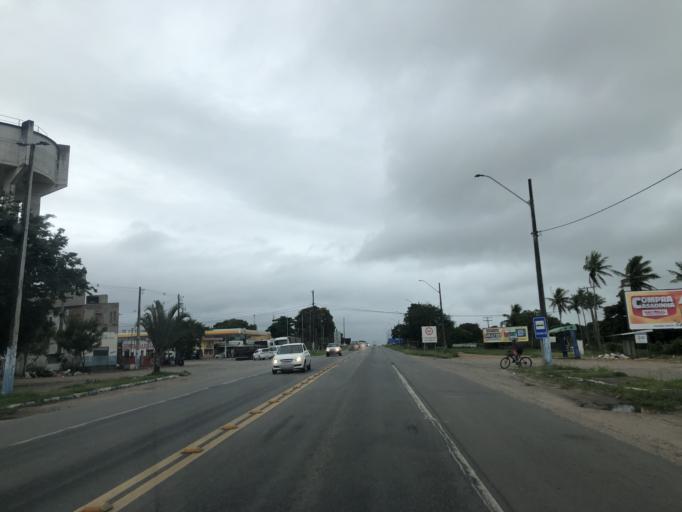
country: BR
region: Bahia
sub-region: Cruz Das Almas
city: Cruz das Almas
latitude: -12.6014
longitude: -39.0506
